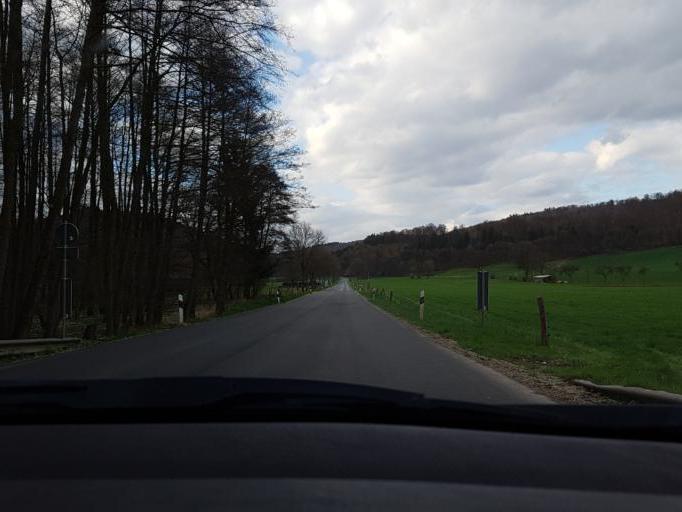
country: DE
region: Lower Saxony
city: Bodenfelde
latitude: 51.6500
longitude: 9.5488
